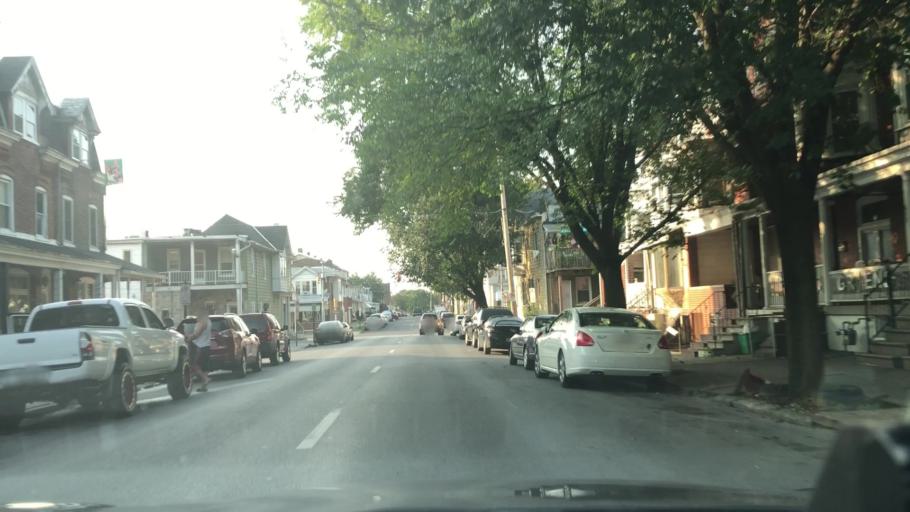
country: US
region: Pennsylvania
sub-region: Lehigh County
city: Allentown
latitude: 40.6094
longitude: -75.4821
